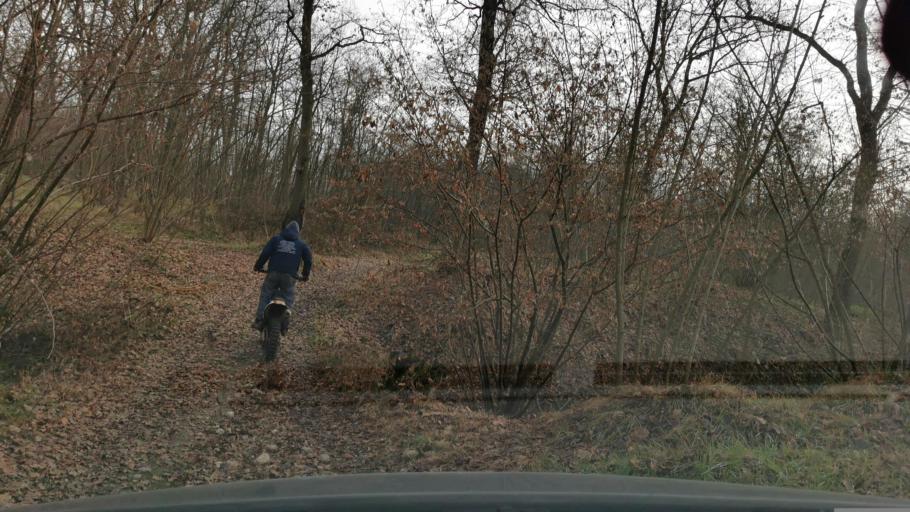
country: IT
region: Piedmont
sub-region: Provincia di Torino
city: San Benigno Canavese
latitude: 45.2510
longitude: 7.7991
